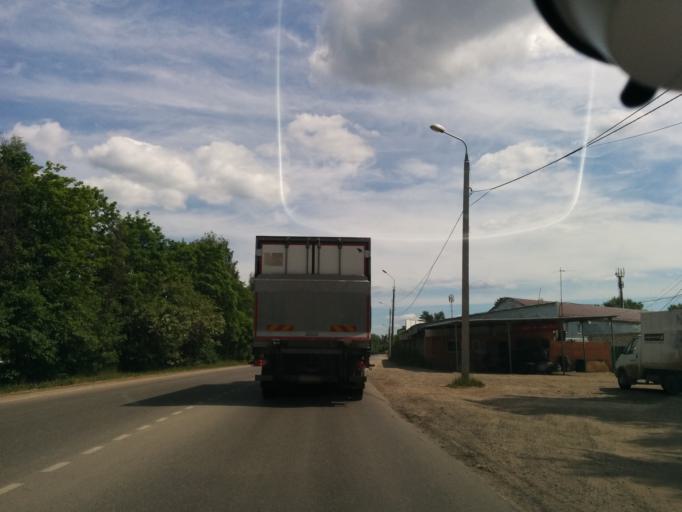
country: RU
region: Perm
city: Overyata
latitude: 58.0158
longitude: 55.9606
